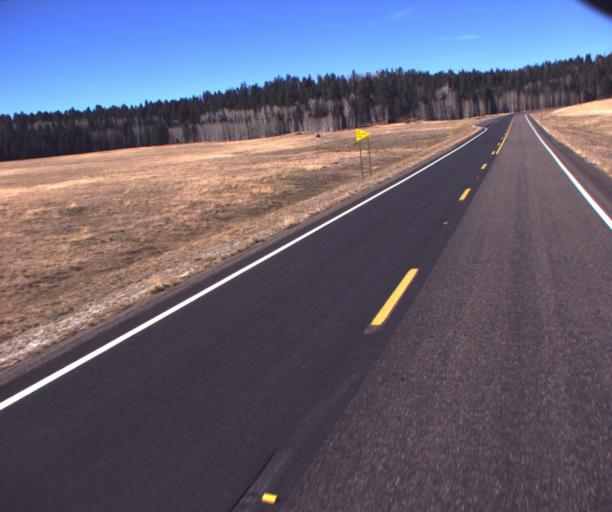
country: US
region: Arizona
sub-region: Coconino County
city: Grand Canyon
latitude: 36.5021
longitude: -112.1384
